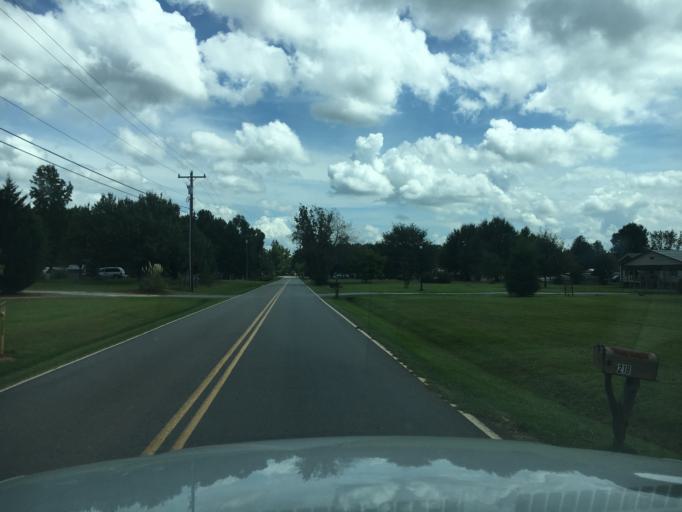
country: US
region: South Carolina
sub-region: Anderson County
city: Belton
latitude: 34.5533
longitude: -82.4658
